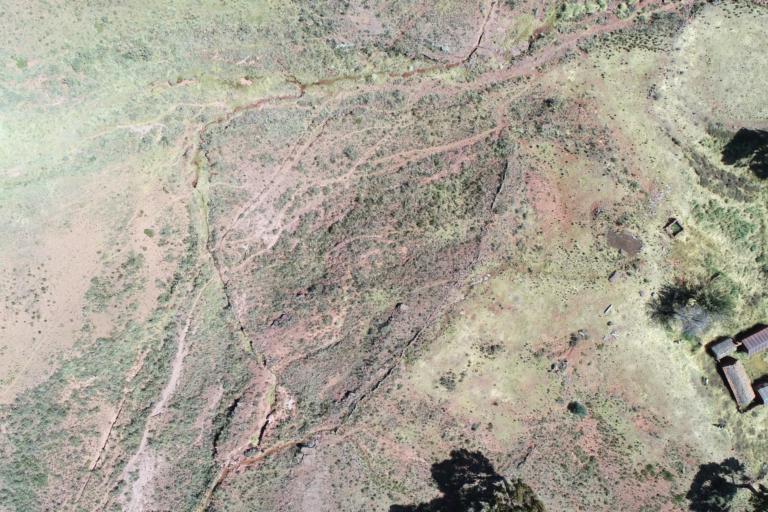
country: BO
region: La Paz
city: Tiahuanaco
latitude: -16.6049
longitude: -68.7727
